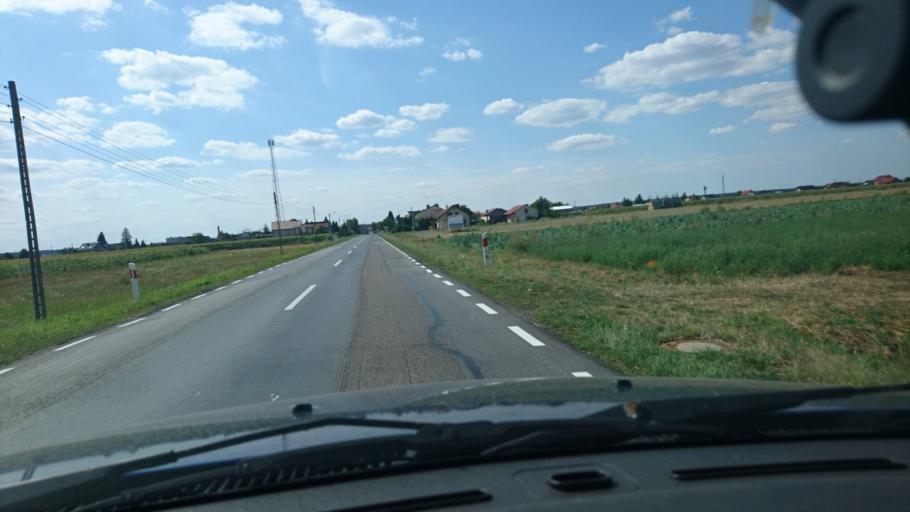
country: PL
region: Greater Poland Voivodeship
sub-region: Powiat krotoszynski
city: Sulmierzyce
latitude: 51.6054
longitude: 17.5464
